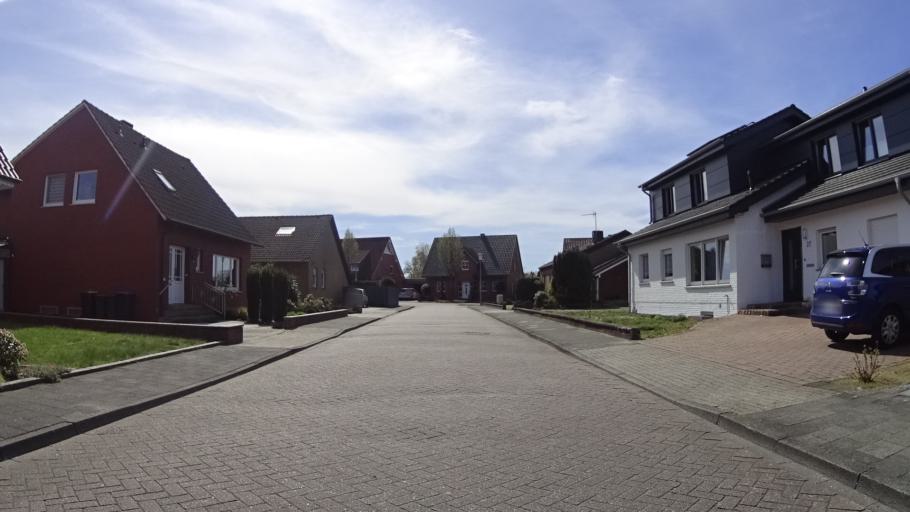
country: DE
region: North Rhine-Westphalia
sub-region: Regierungsbezirk Munster
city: Dreierwalde
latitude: 52.3001
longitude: 7.4713
